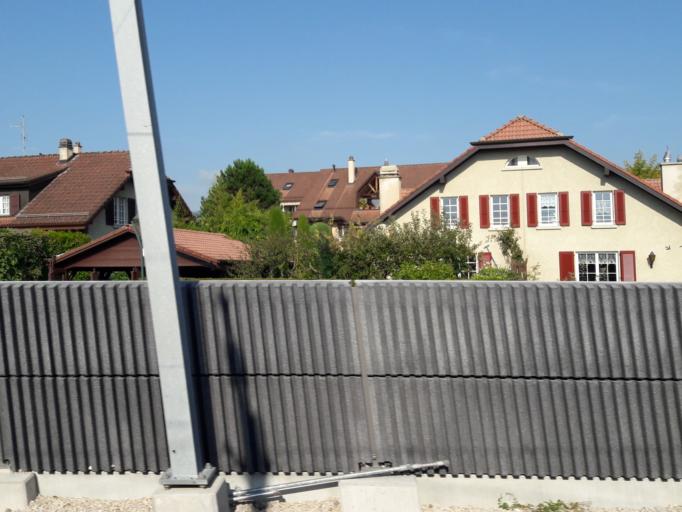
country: CH
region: Vaud
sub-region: Nyon District
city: Gland
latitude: 46.4223
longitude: 6.2716
